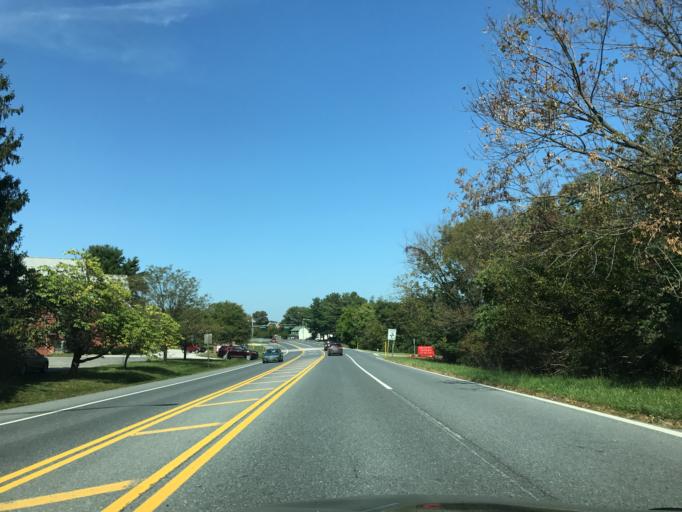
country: US
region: Maryland
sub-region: Howard County
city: Ilchester
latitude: 39.2050
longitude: -76.7959
